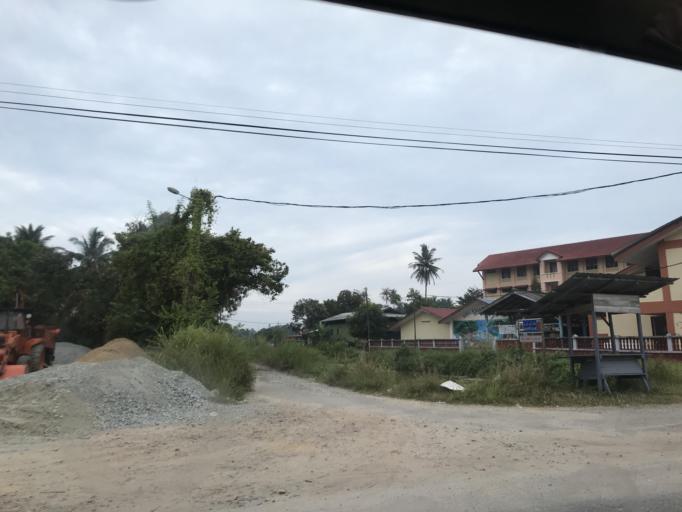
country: MY
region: Kelantan
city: Kota Bharu
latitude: 6.1449
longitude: 102.2224
